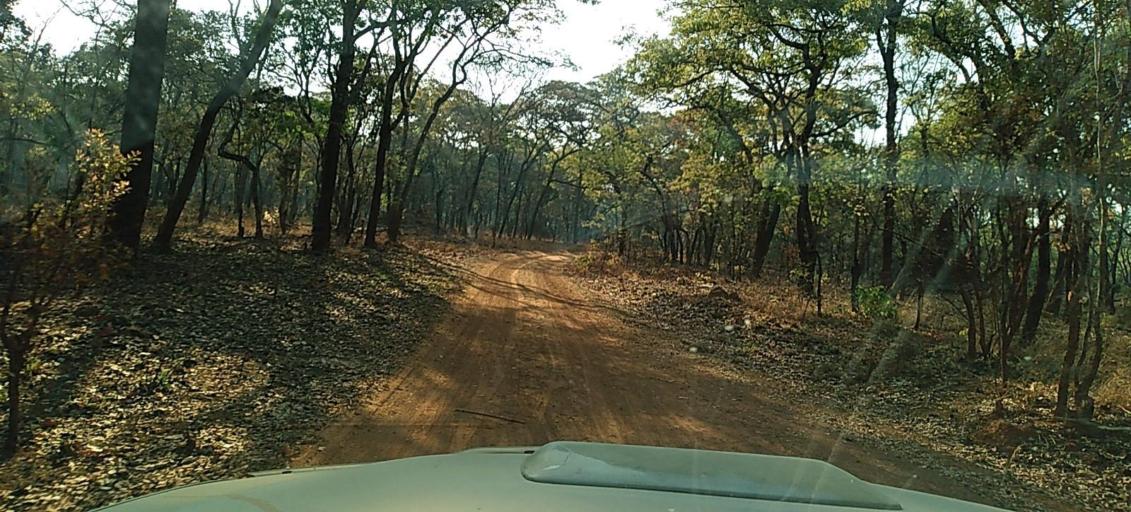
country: ZM
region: North-Western
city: Kasempa
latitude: -13.1671
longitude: 25.8909
